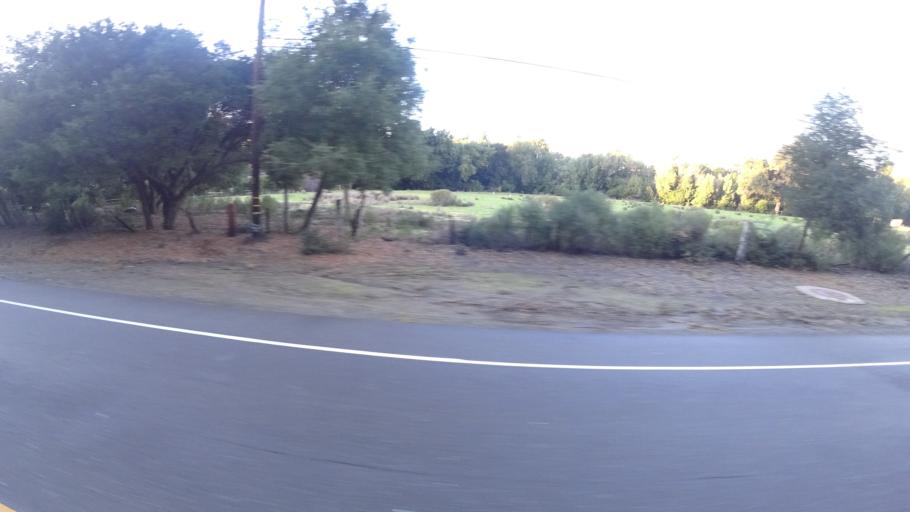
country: US
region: California
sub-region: Alameda County
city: Dublin
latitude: 37.6950
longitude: -121.9462
